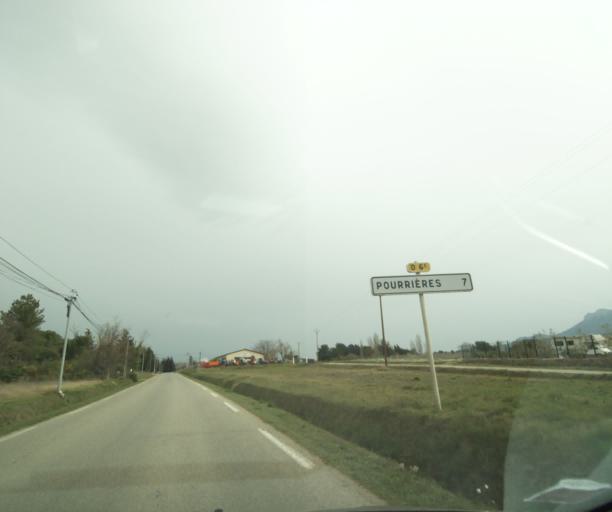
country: FR
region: Provence-Alpes-Cote d'Azur
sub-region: Departement des Bouches-du-Rhone
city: Trets
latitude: 43.4544
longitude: 5.6946
